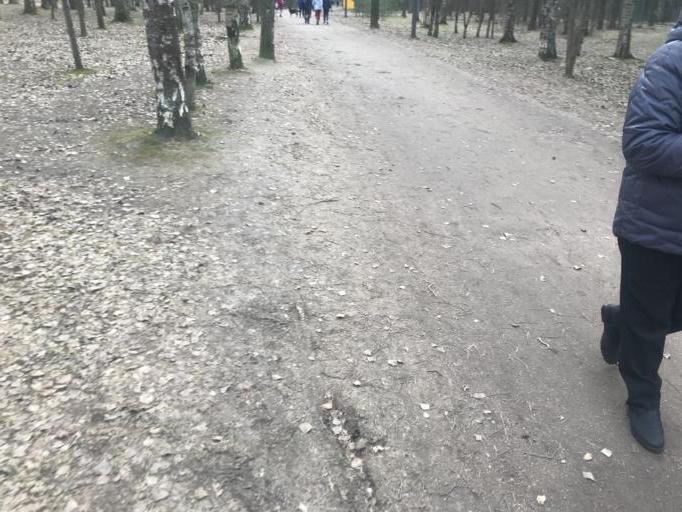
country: RU
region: St.-Petersburg
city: Sosnovka
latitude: 60.0168
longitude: 30.3482
